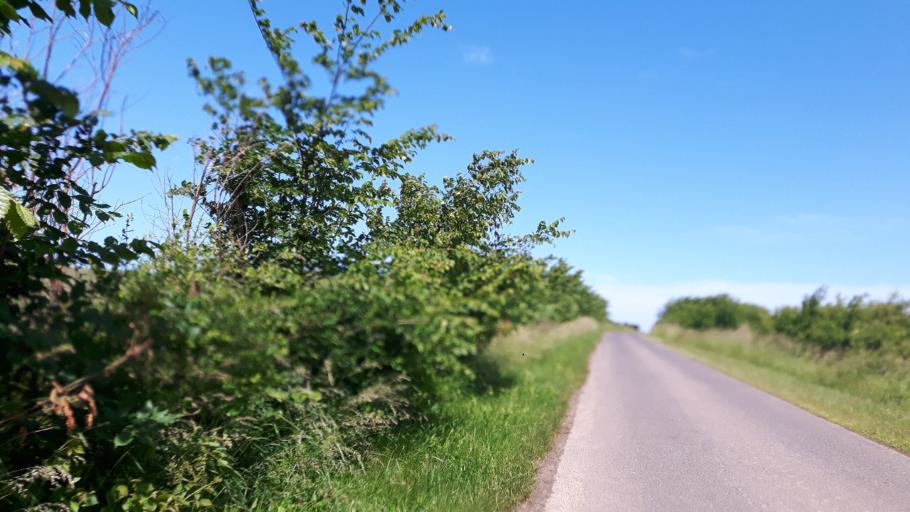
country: PL
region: West Pomeranian Voivodeship
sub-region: Powiat gryficki
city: Mrzezyno
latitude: 54.1006
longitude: 15.3037
